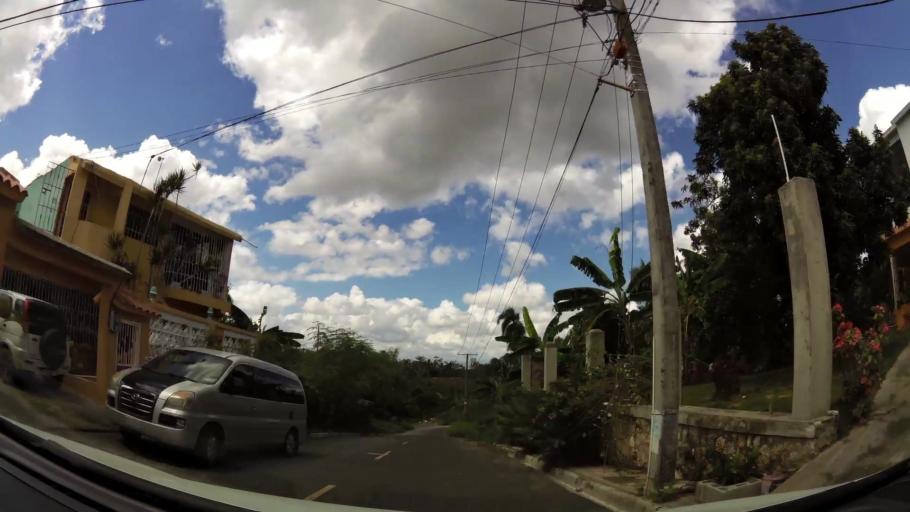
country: DO
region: Nacional
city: La Agustina
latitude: 18.5224
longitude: -69.9207
